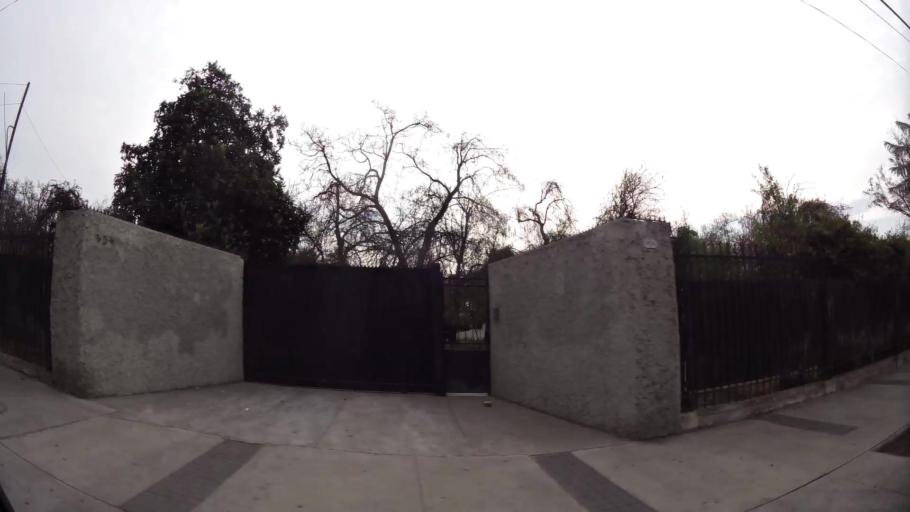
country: CL
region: Santiago Metropolitan
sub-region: Provincia de Santiago
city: Lo Prado
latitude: -33.5225
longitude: -70.7574
